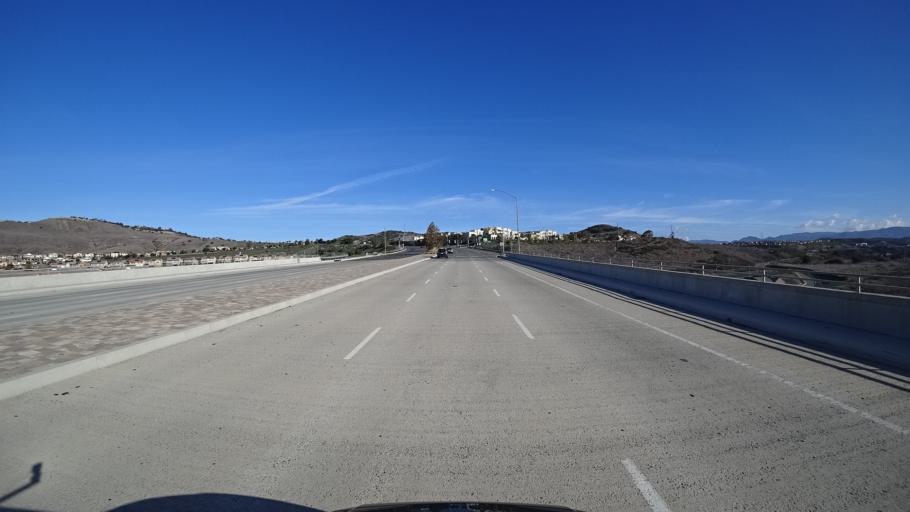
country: US
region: California
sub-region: Orange County
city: San Juan Capistrano
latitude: 33.5241
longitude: -117.6193
